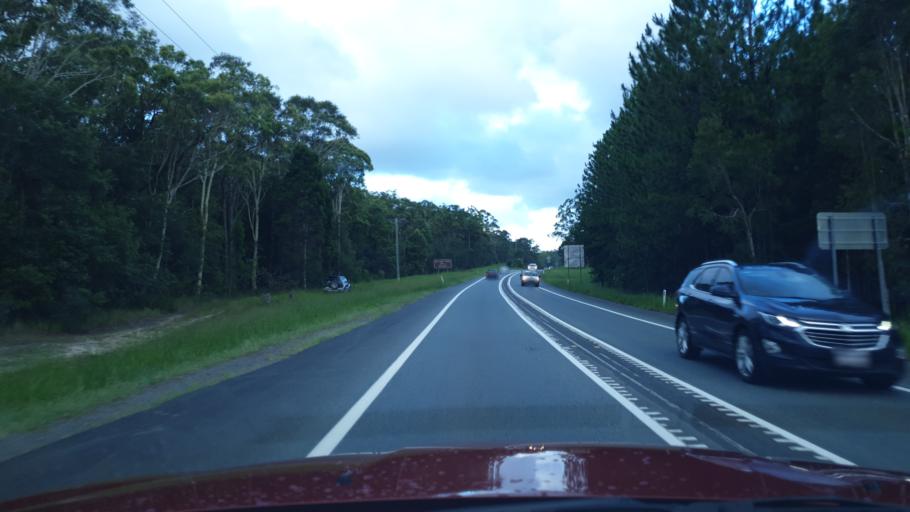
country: AU
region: Queensland
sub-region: Sunshine Coast
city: Little Mountain
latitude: -26.7974
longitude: 152.9906
